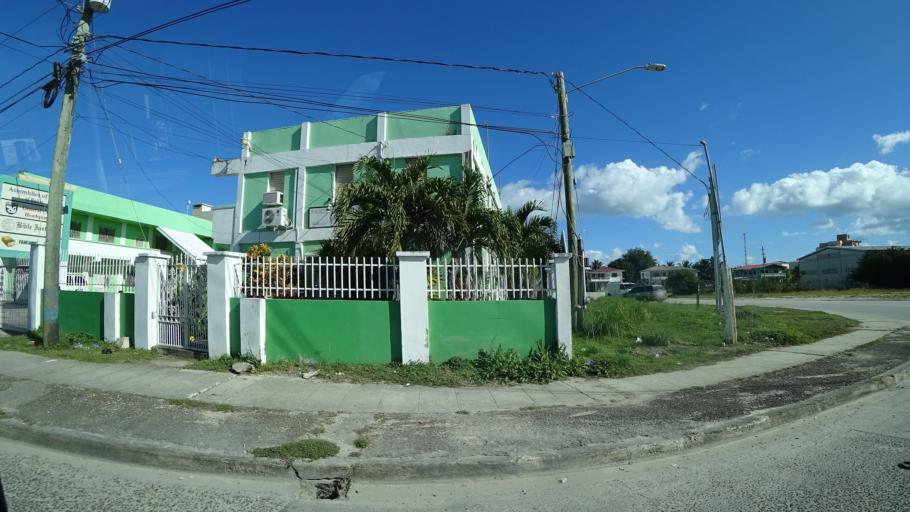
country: BZ
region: Belize
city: Belize City
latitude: 17.5069
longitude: -88.2029
